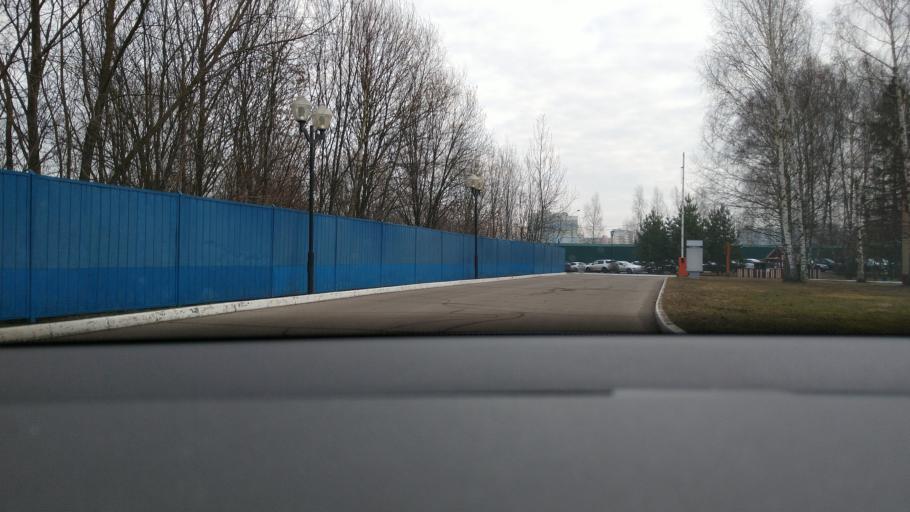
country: RU
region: Moskovskaya
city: Vatutinki
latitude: 55.5156
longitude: 37.3353
